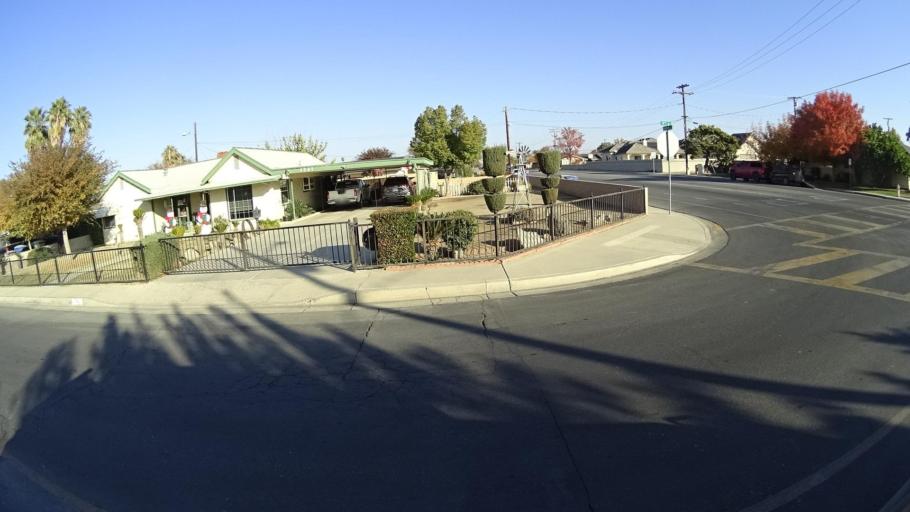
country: US
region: California
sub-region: Kern County
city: Delano
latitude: 35.7686
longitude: -119.2323
